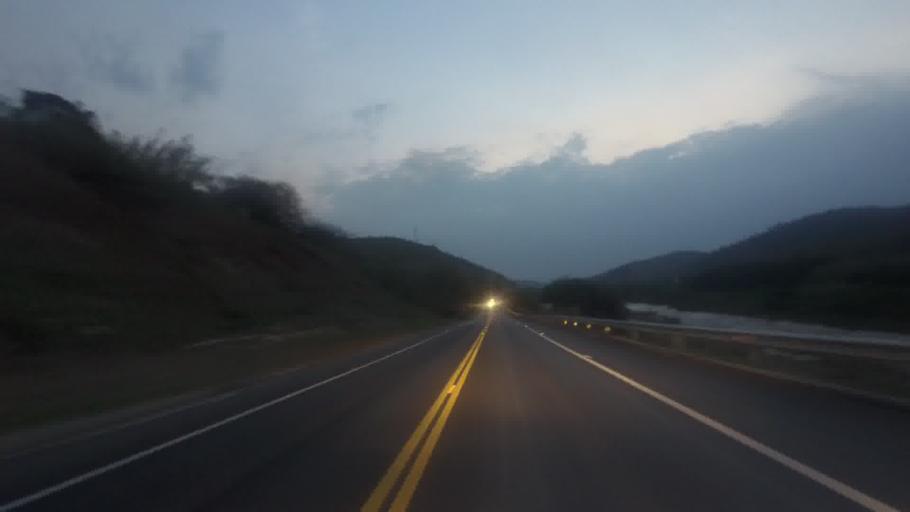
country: BR
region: Minas Gerais
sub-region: Alem Paraiba
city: Alem Paraiba
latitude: -21.9280
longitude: -42.7824
